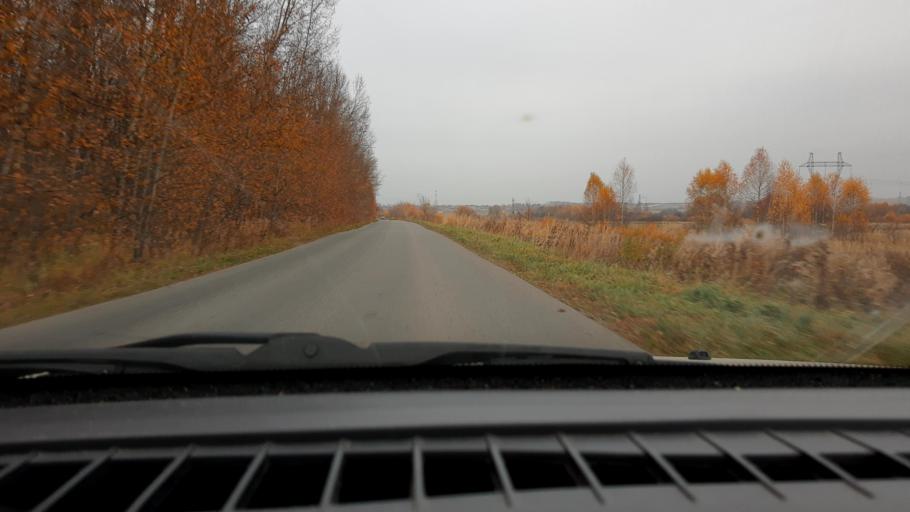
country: RU
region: Nizjnij Novgorod
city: Burevestnik
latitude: 56.0438
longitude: 43.8512
